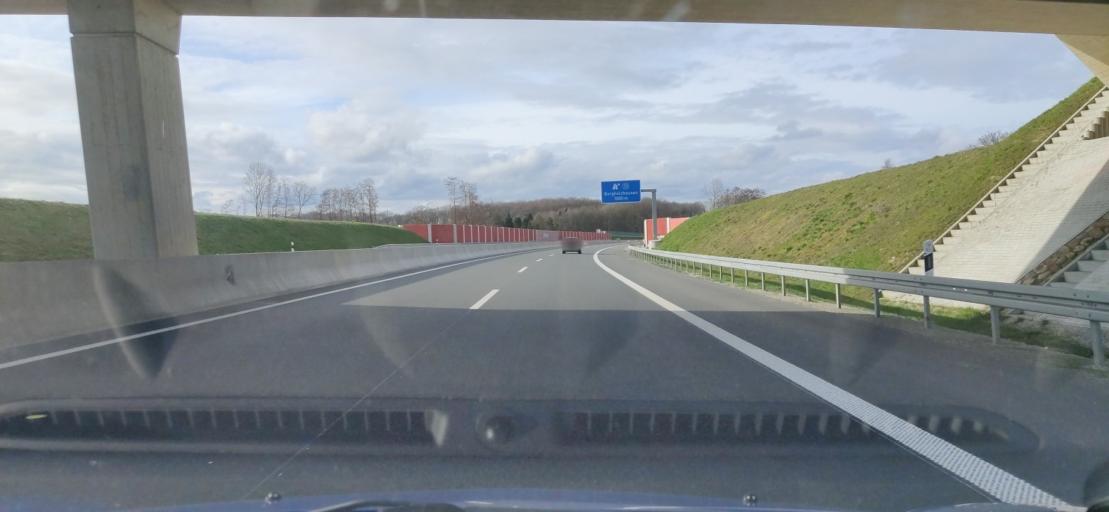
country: DE
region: North Rhine-Westphalia
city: Borgholzhausen
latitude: 52.0686
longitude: 8.2626
